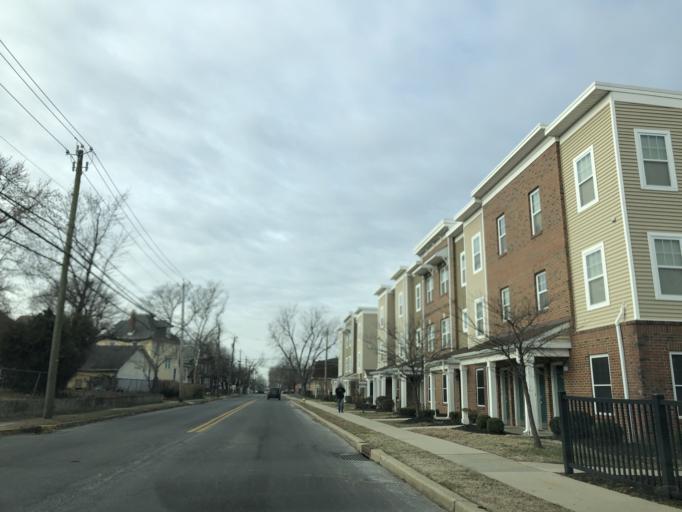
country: US
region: New Jersey
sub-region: Camden County
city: Wood-Lynne
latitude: 39.9202
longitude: -75.0946
